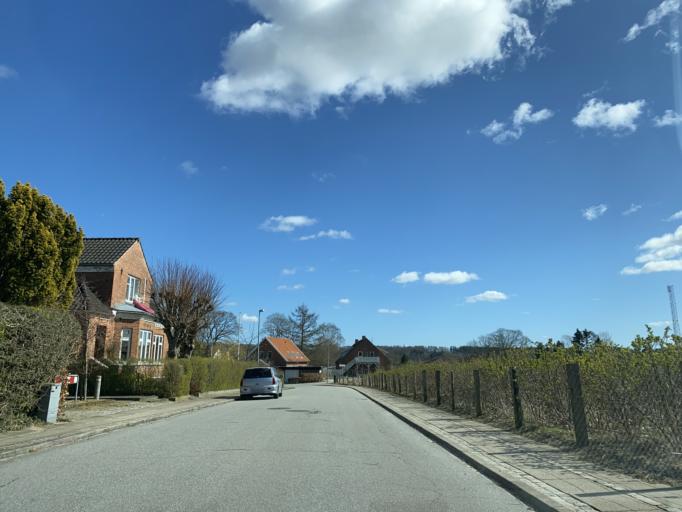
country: DK
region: Central Jutland
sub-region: Randers Kommune
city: Langa
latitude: 56.3858
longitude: 9.8922
